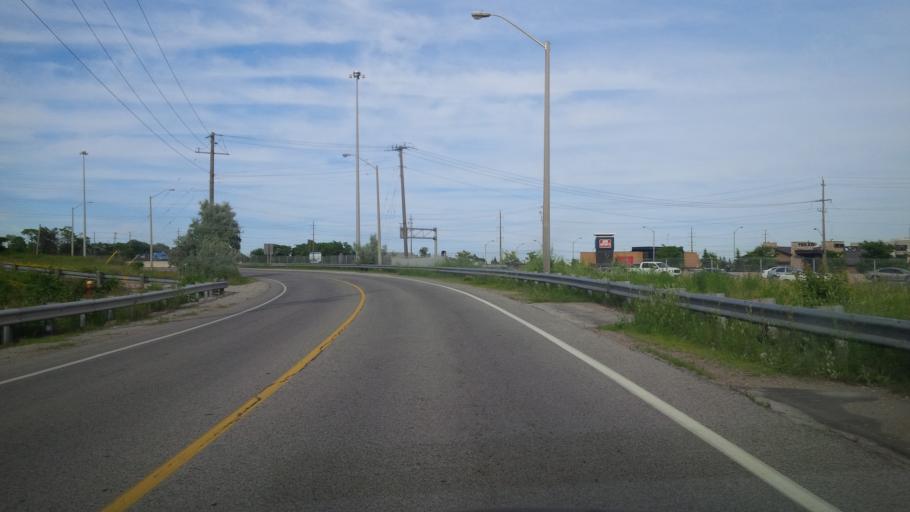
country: CA
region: Ontario
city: Burlington
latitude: 43.3553
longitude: -79.8016
